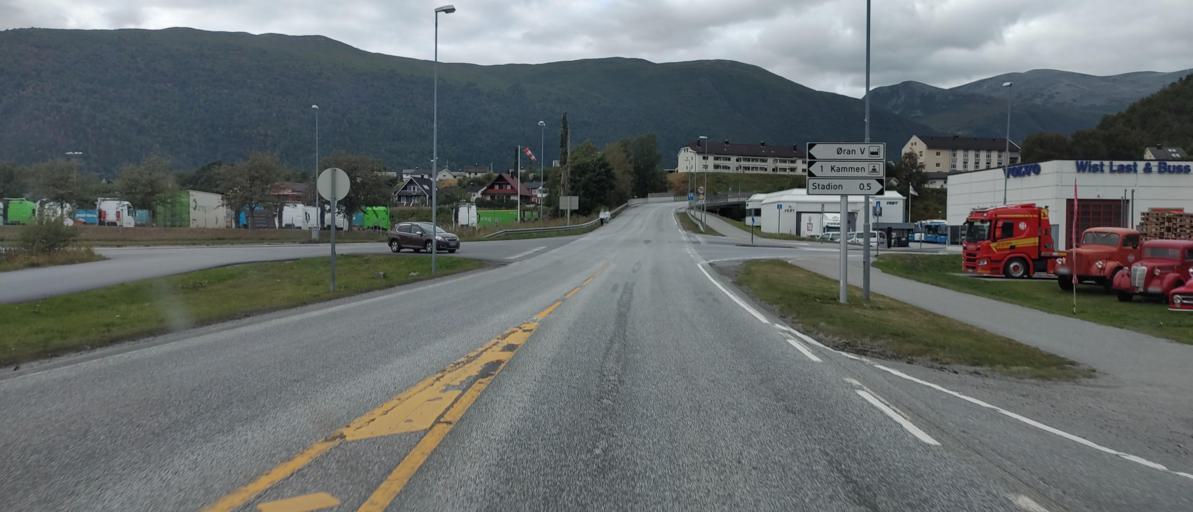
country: NO
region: More og Romsdal
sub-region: Rauma
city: Andalsnes
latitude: 62.5596
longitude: 7.6837
